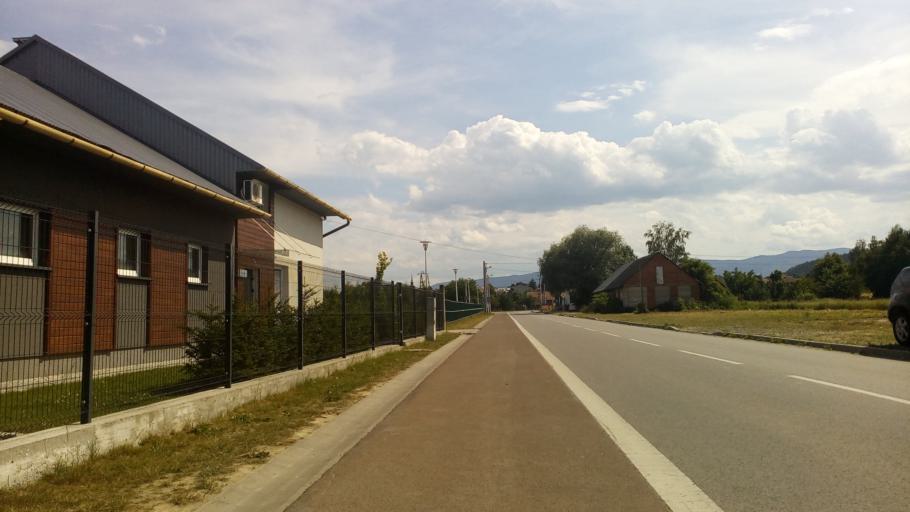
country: PL
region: Lesser Poland Voivodeship
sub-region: Powiat nowosadecki
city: Stary Sacz
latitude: 49.5717
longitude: 20.6365
